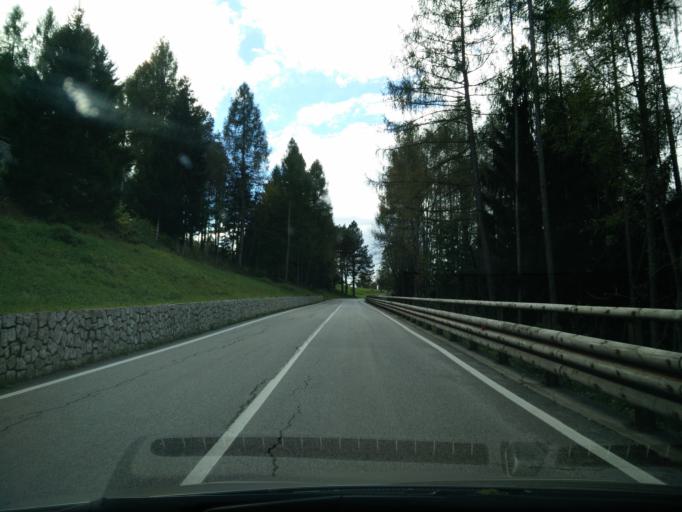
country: IT
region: Veneto
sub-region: Provincia di Belluno
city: Lorenzago di Cadore
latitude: 46.4841
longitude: 12.4615
